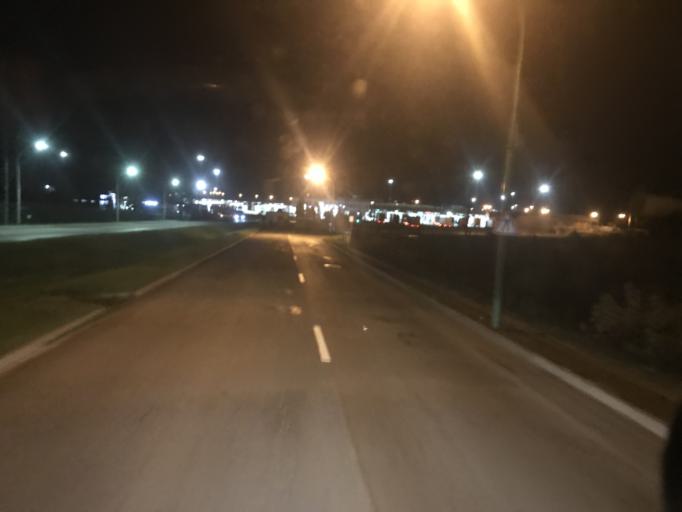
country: PL
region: Lublin Voivodeship
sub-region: Powiat bialski
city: Terespol
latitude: 52.1190
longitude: 23.5684
